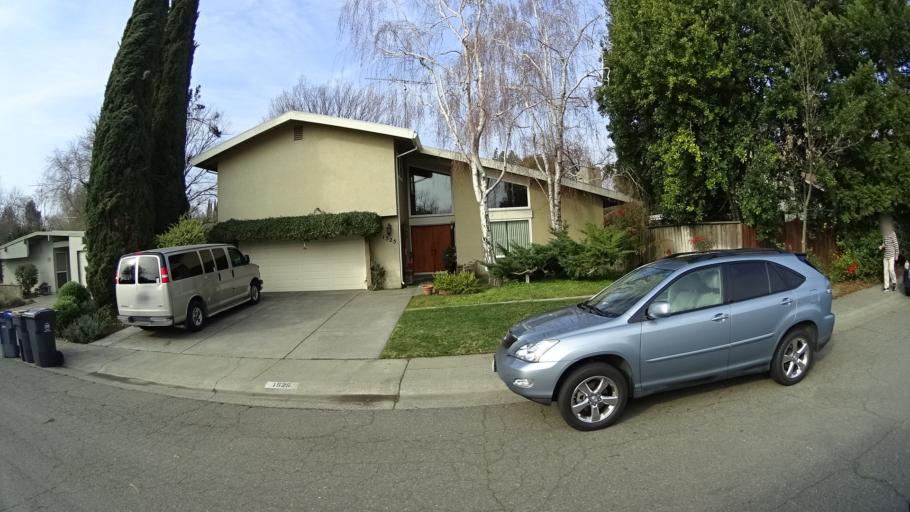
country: US
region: California
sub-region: Yolo County
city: Davis
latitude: 38.5571
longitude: -121.7605
